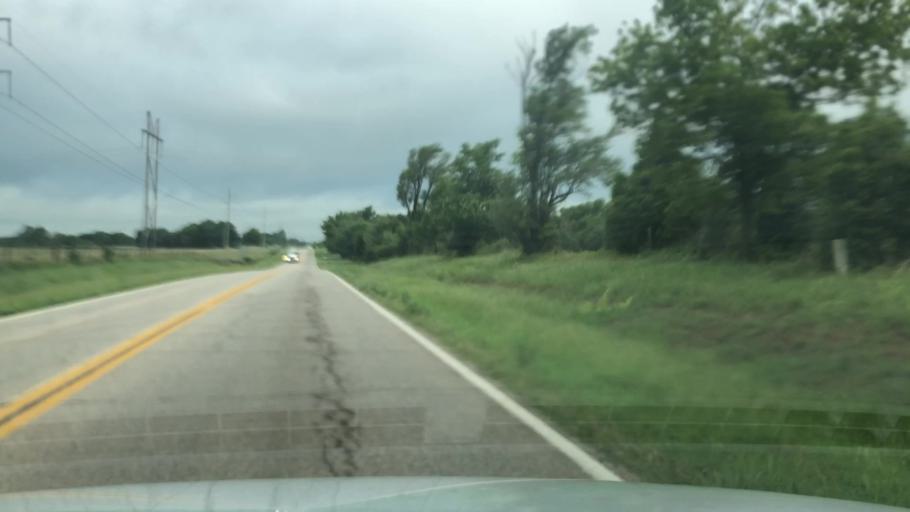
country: US
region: Oklahoma
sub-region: Nowata County
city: Nowata
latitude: 36.7136
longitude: -95.6686
